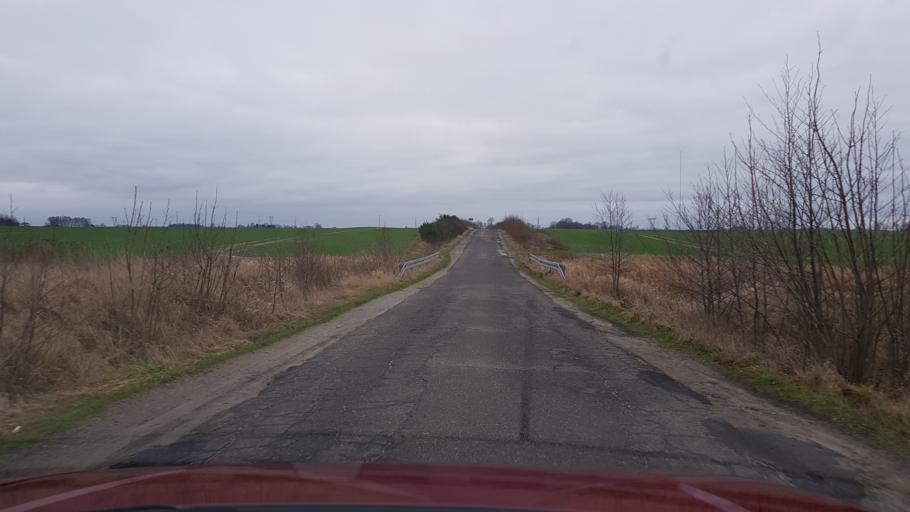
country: PL
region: West Pomeranian Voivodeship
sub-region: Powiat koszalinski
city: Mielno
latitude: 54.1577
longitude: 16.0337
